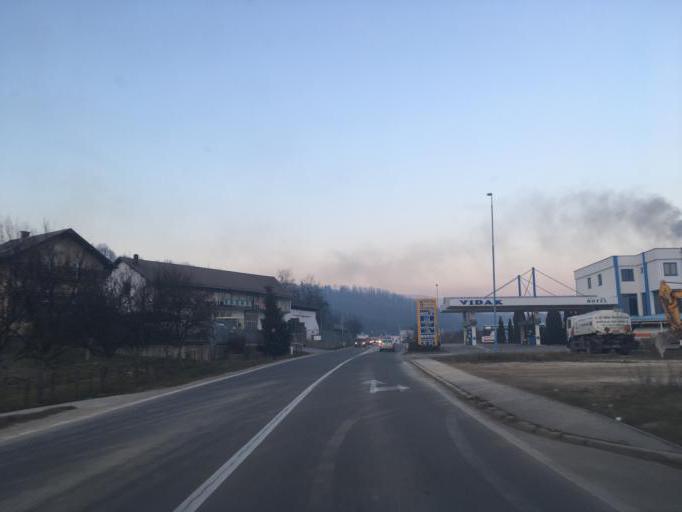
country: BA
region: Federation of Bosnia and Herzegovina
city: Novi Travnik
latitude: 44.1831
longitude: 17.6708
